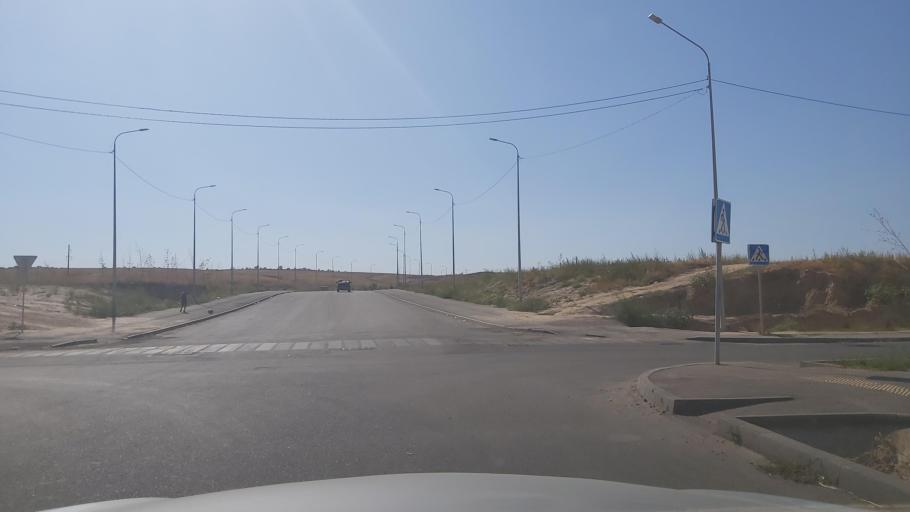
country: KZ
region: Almaty Oblysy
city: Burunday
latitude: 43.3213
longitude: 76.8390
